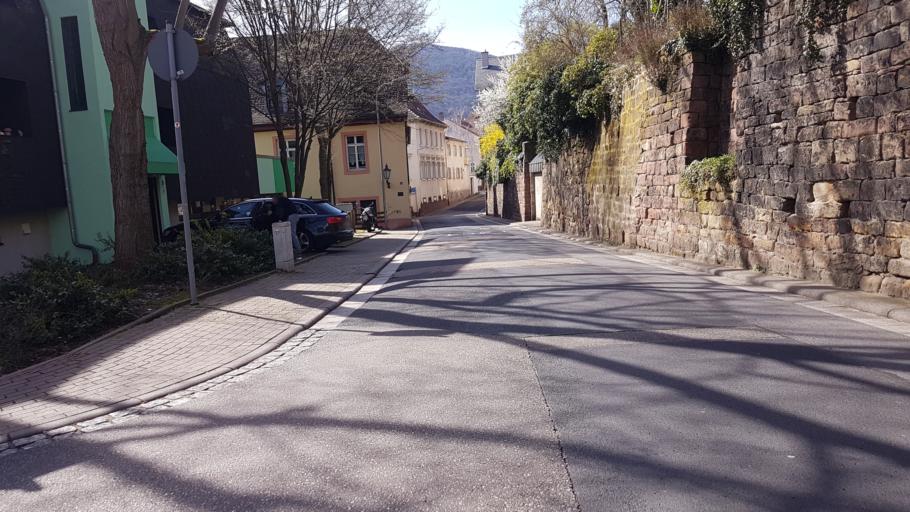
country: DE
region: Rheinland-Pfalz
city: Neustadt
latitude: 49.3558
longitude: 8.1341
